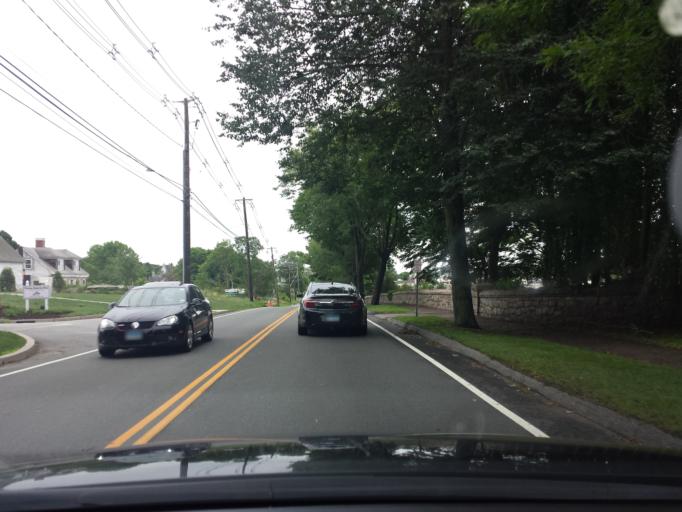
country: US
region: Connecticut
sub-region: New London County
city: Mystic
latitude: 41.3682
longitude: -71.9622
